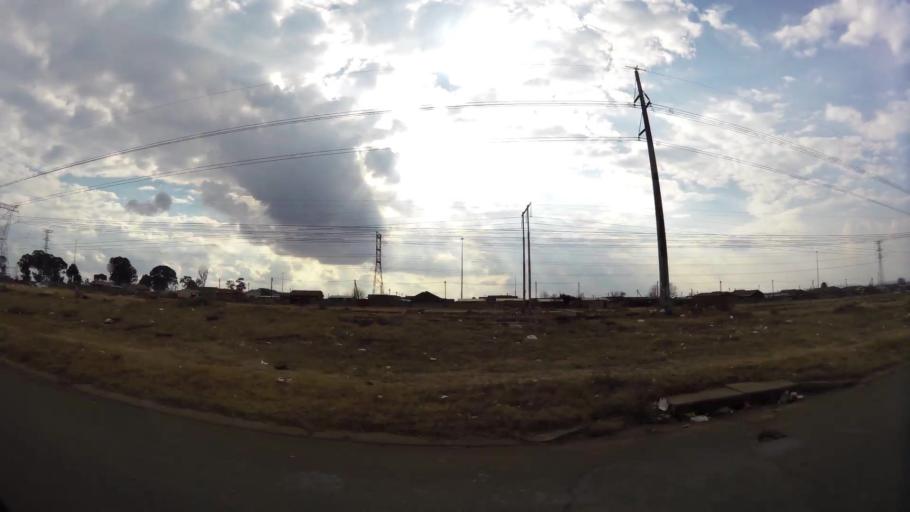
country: ZA
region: Gauteng
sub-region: Sedibeng District Municipality
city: Vanderbijlpark
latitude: -26.6820
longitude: 27.8692
